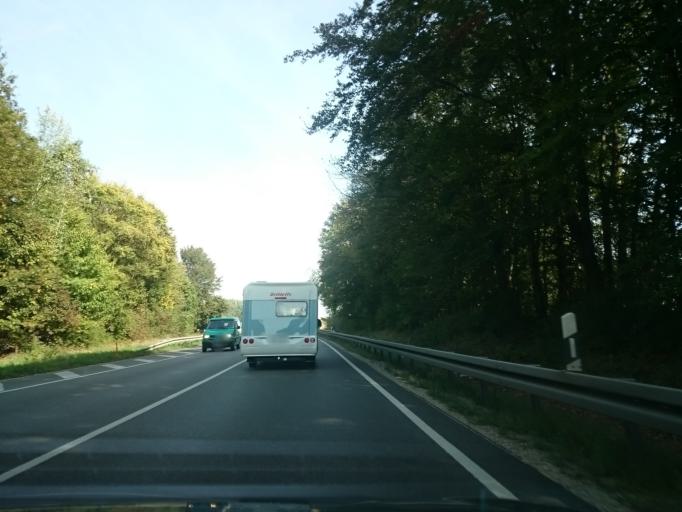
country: DE
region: Bavaria
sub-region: Swabia
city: Aichach
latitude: 48.4580
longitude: 11.1482
